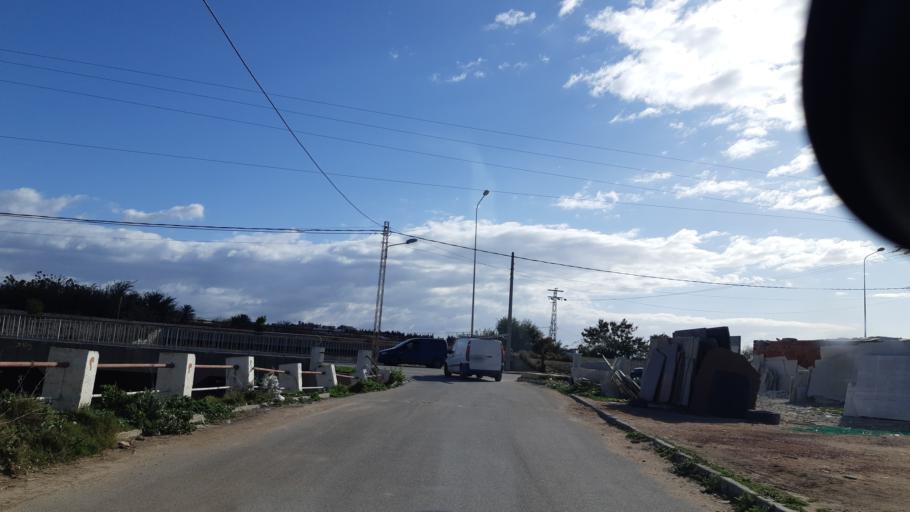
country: TN
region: Susah
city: Akouda
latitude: 35.8707
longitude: 10.5493
